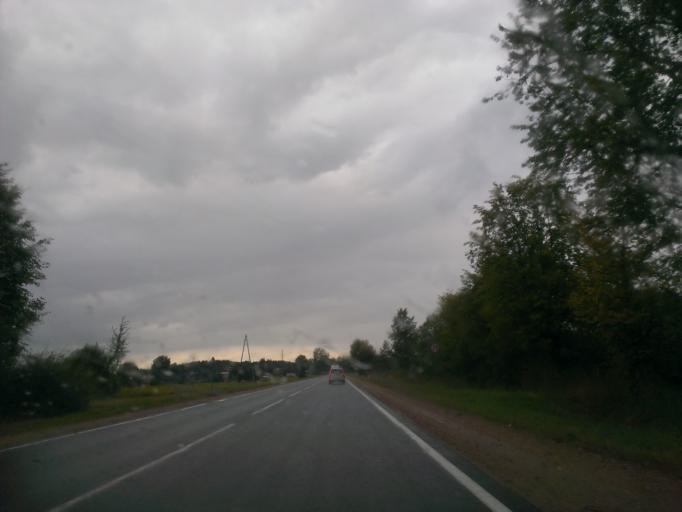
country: LV
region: Ogre
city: Ogre
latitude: 56.7738
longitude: 24.6625
